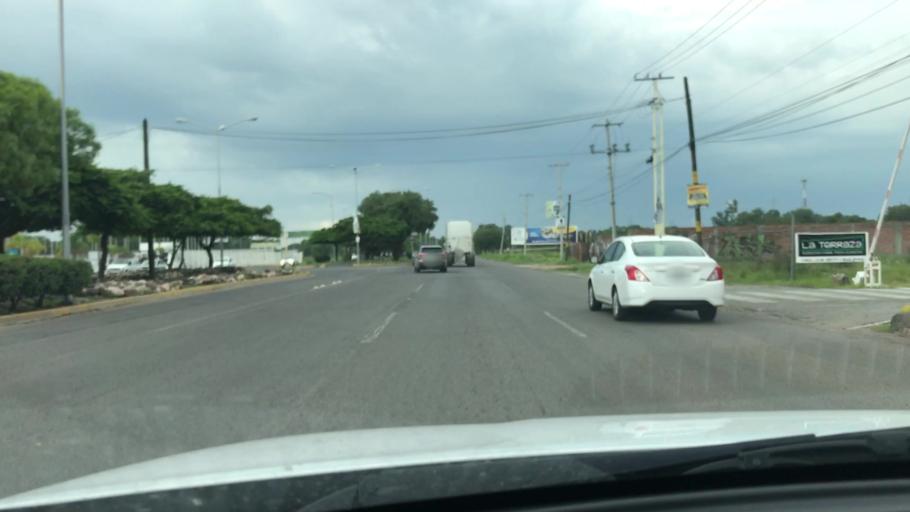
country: MX
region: Guanajuato
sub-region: Celaya
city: La Trinidad
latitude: 20.5363
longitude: -100.7819
